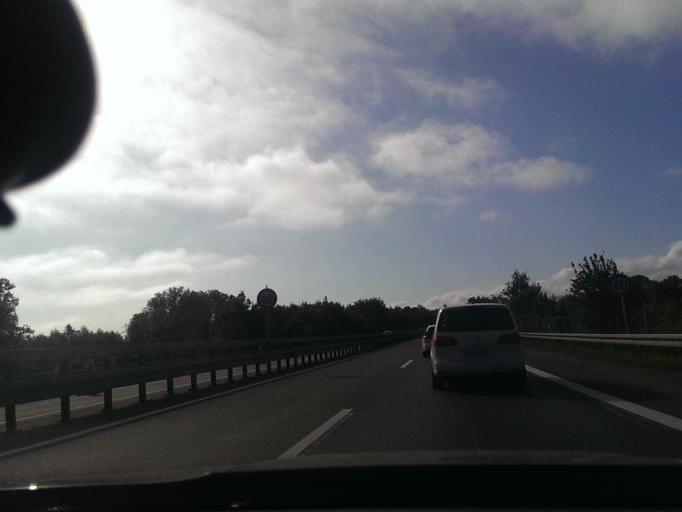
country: DE
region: Lower Saxony
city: Vienenburg
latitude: 51.9552
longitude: 10.5814
